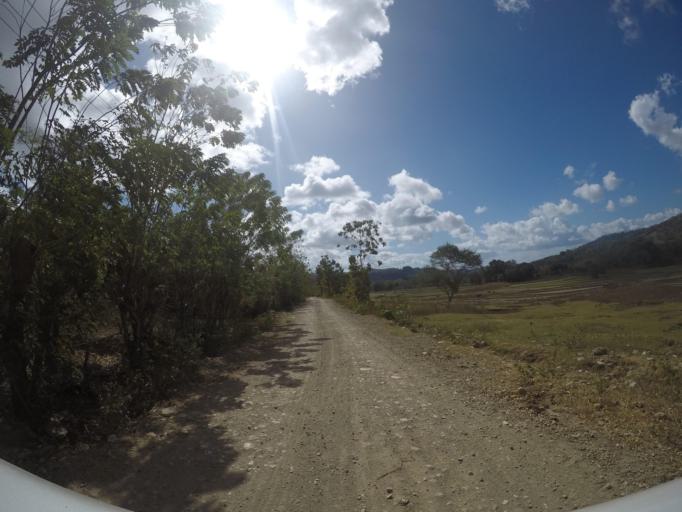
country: TL
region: Lautem
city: Lospalos
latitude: -8.5208
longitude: 126.8400
